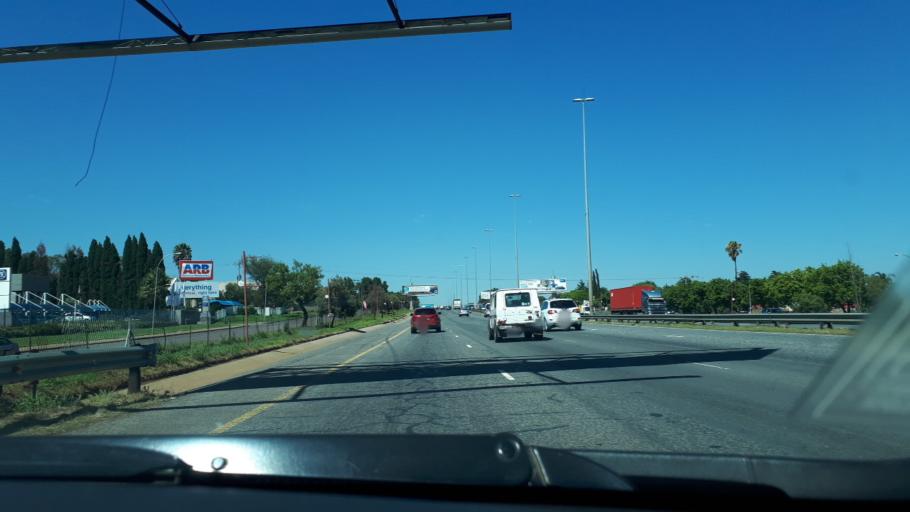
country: ZA
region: Gauteng
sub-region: City of Johannesburg Metropolitan Municipality
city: Modderfontein
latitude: -26.1482
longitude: 28.1771
